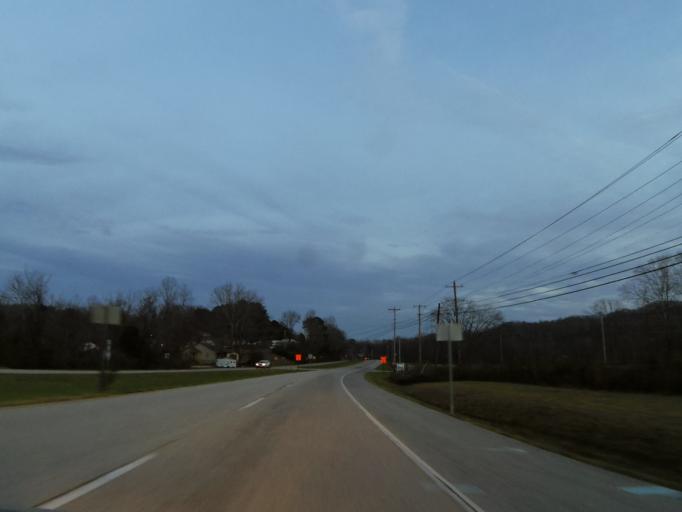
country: US
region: Tennessee
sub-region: Roane County
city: Harriman
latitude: 35.9698
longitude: -84.4963
